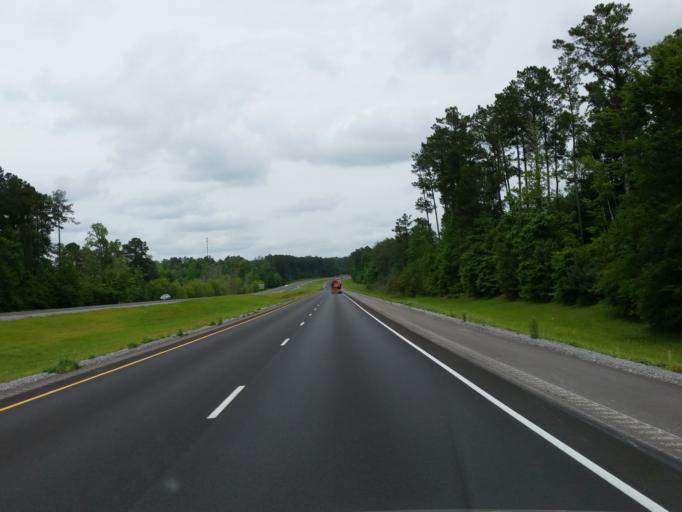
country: US
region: Mississippi
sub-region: Jones County
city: Sharon
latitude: 31.8651
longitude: -89.0463
